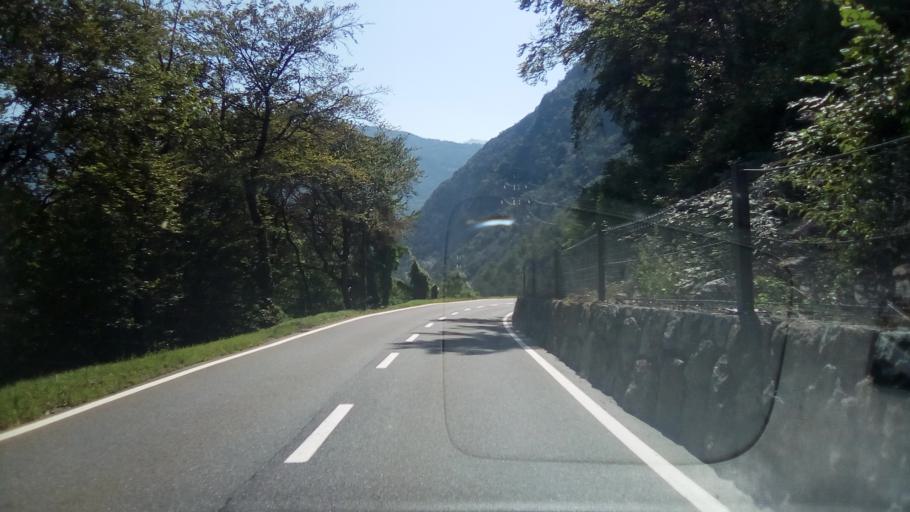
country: CH
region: Valais
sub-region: Saint-Maurice District
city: Vernayaz
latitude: 46.1156
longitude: 7.0497
